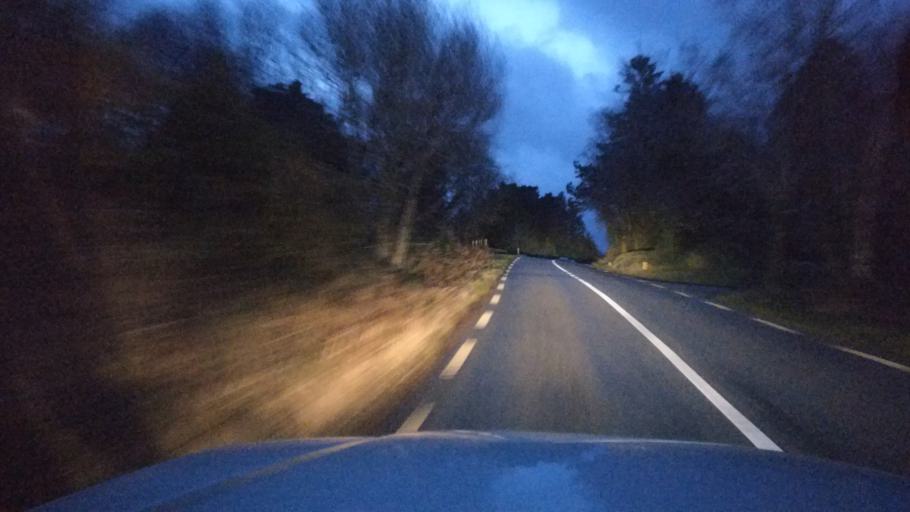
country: IE
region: Connaught
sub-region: County Galway
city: Oughterard
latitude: 53.3878
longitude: -9.5501
